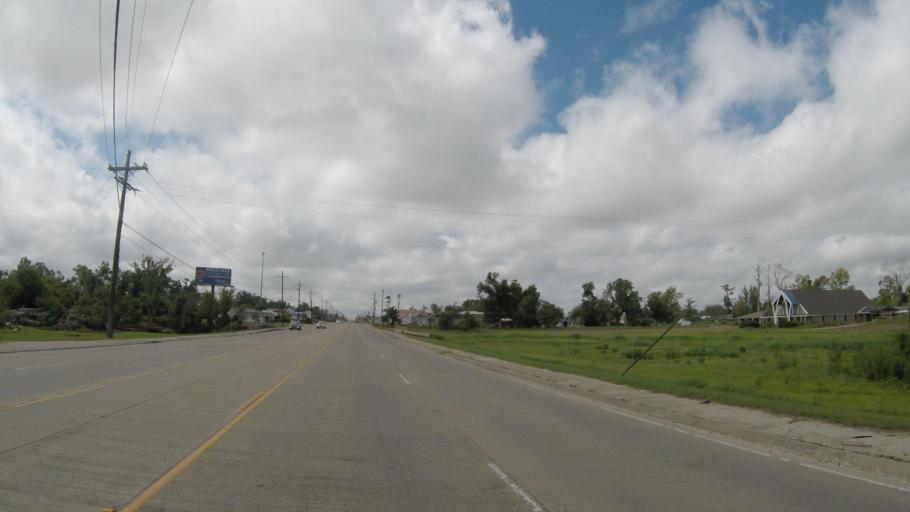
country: US
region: Louisiana
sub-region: Calcasieu Parish
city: Westlake
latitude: 30.2629
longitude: -93.2582
